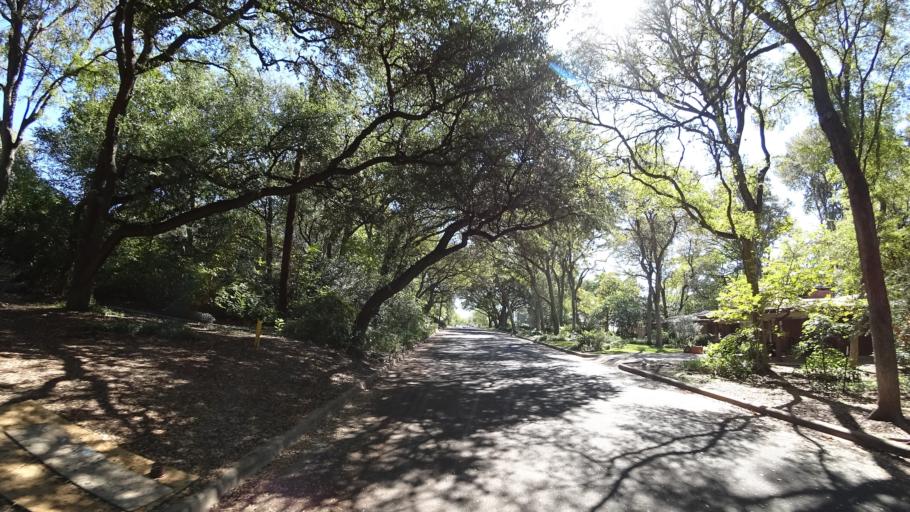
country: US
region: Texas
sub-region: Travis County
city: West Lake Hills
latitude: 30.3170
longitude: -97.7706
